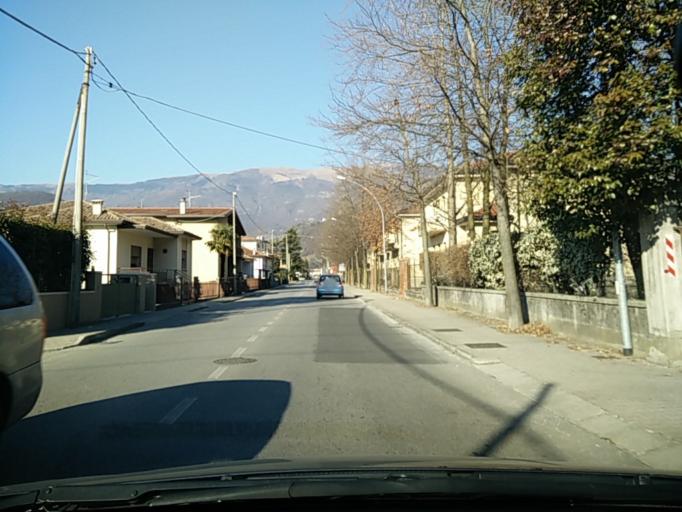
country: IT
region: Veneto
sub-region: Provincia di Treviso
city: Vittorio Veneto
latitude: 45.9899
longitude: 12.3064
